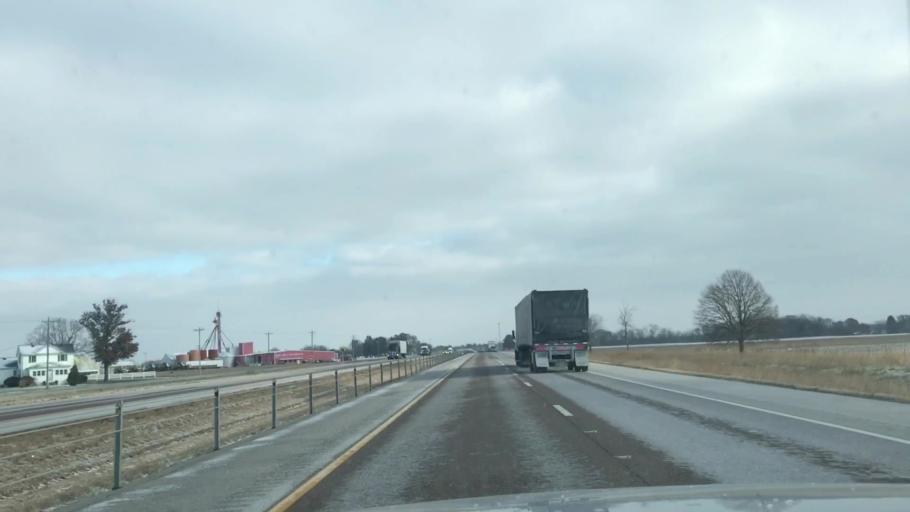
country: US
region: Illinois
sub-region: Madison County
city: Worden
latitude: 38.9214
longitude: -89.8114
